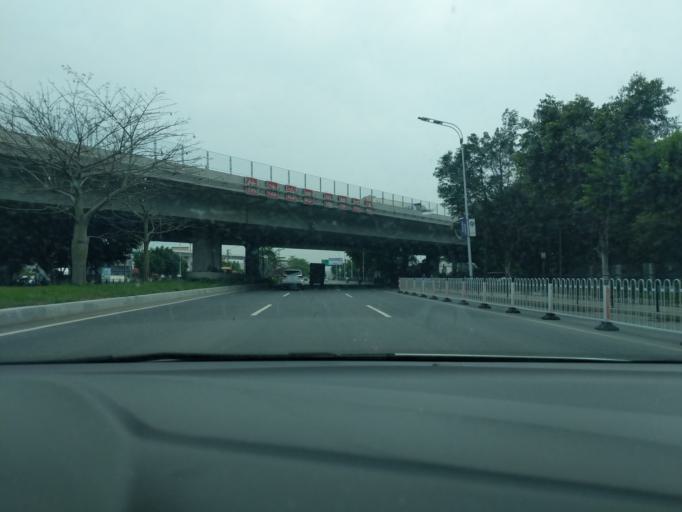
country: CN
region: Guangdong
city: Huangge
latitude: 22.8586
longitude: 113.4869
